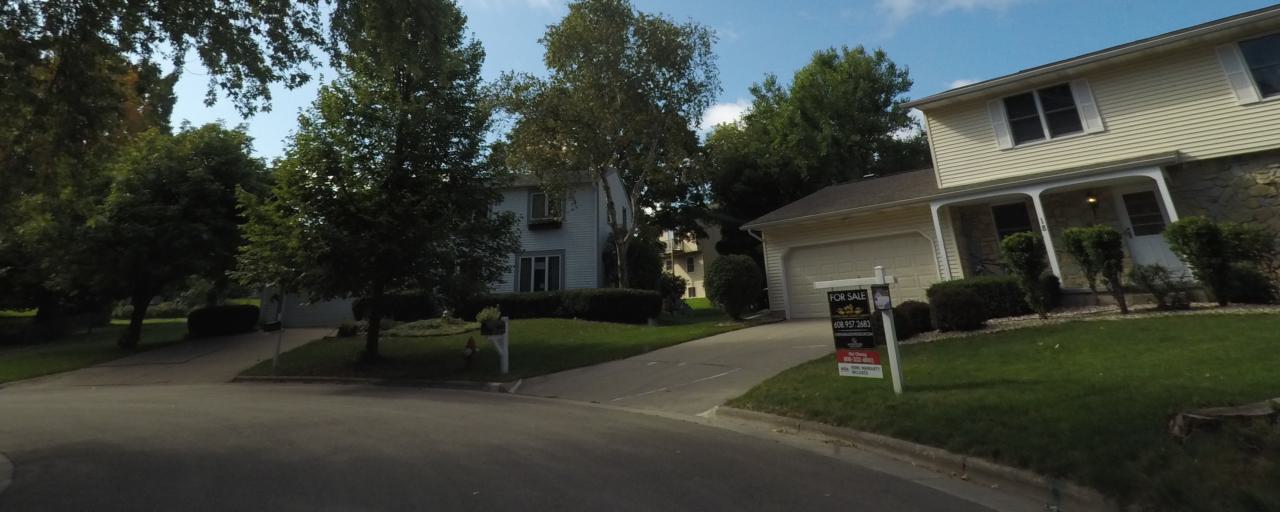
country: US
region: Wisconsin
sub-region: Dane County
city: Middleton
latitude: 43.0776
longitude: -89.5047
